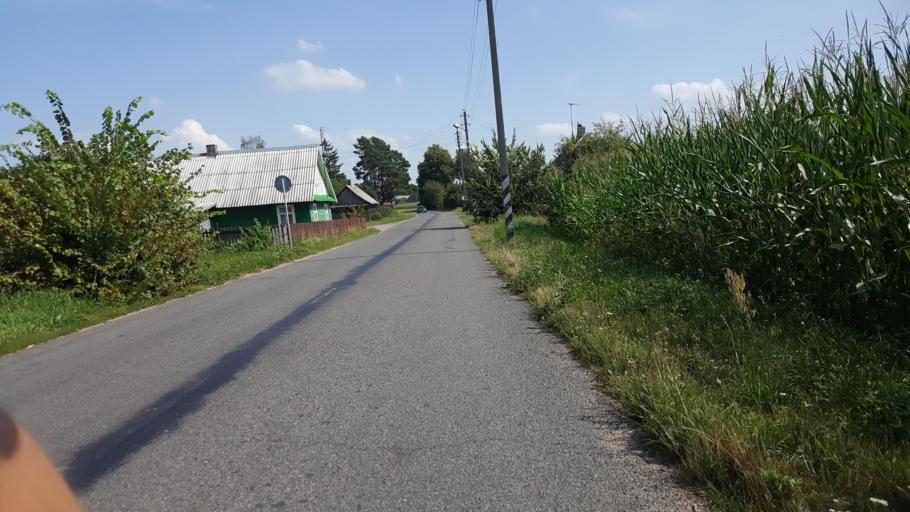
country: BY
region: Brest
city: Kamyanyuki
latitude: 52.5048
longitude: 23.6557
